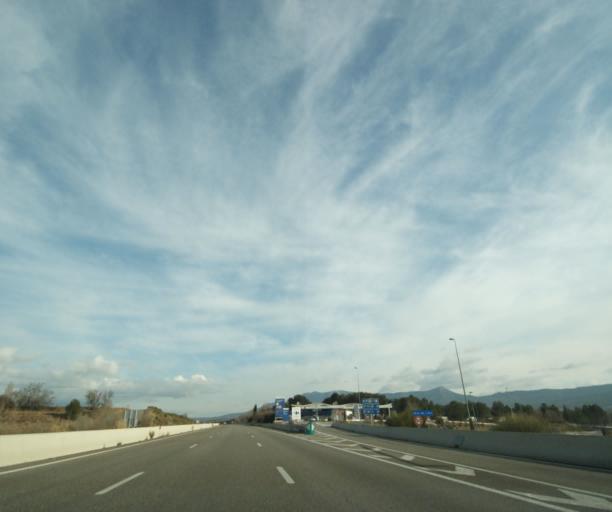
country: FR
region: Provence-Alpes-Cote d'Azur
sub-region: Departement des Bouches-du-Rhone
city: Peynier
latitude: 43.4700
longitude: 5.6525
